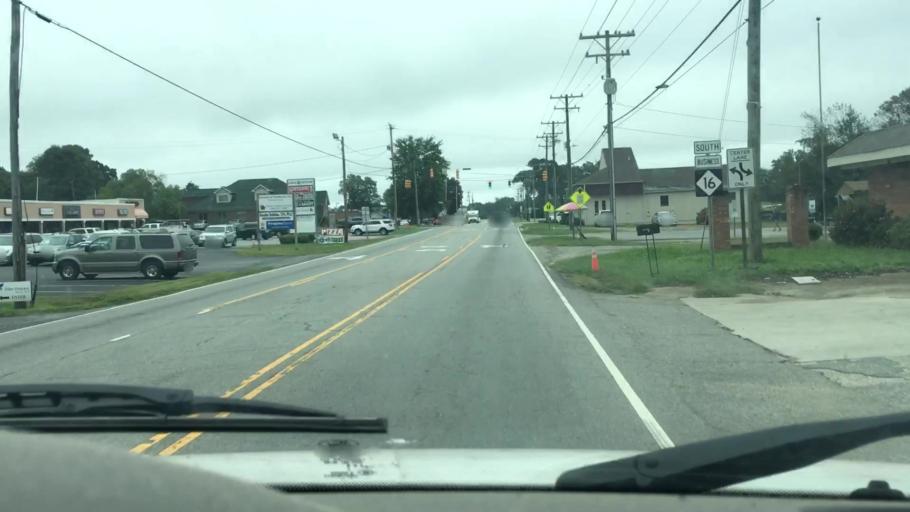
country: US
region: North Carolina
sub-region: Lincoln County
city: Denver
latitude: 35.5317
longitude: -81.0301
